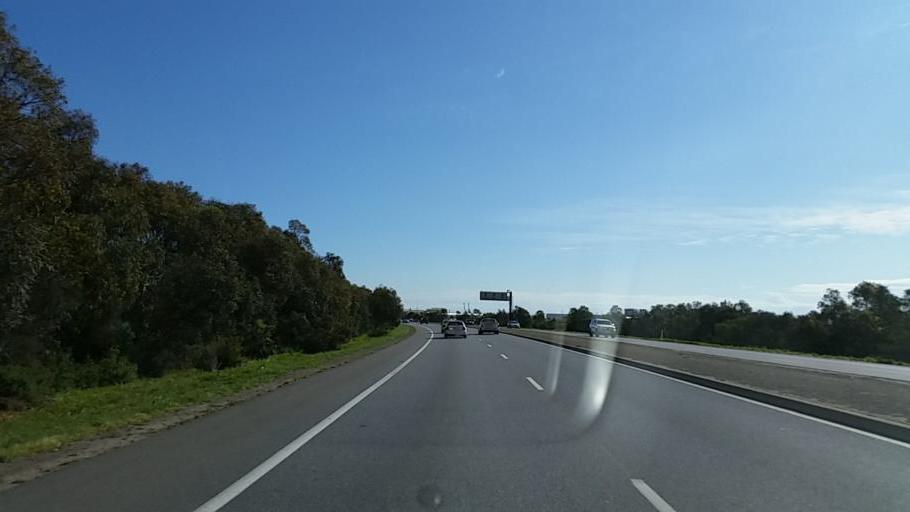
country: AU
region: South Australia
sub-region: Port Adelaide Enfield
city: Alberton
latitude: -34.8346
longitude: 138.5326
